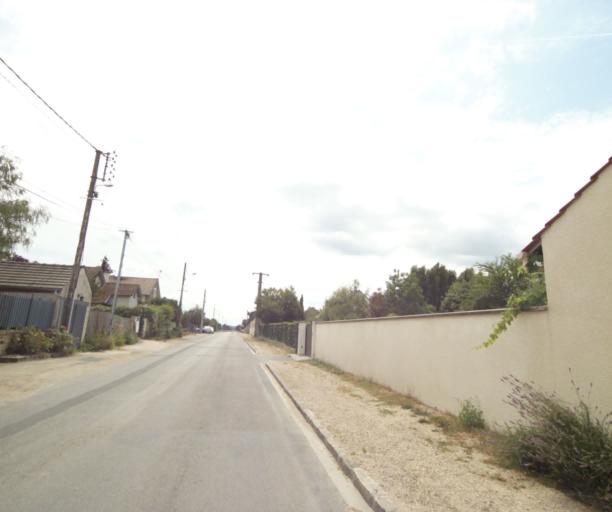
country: FR
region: Ile-de-France
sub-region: Departement de Seine-et-Marne
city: Barbizon
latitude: 48.4309
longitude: 2.5854
